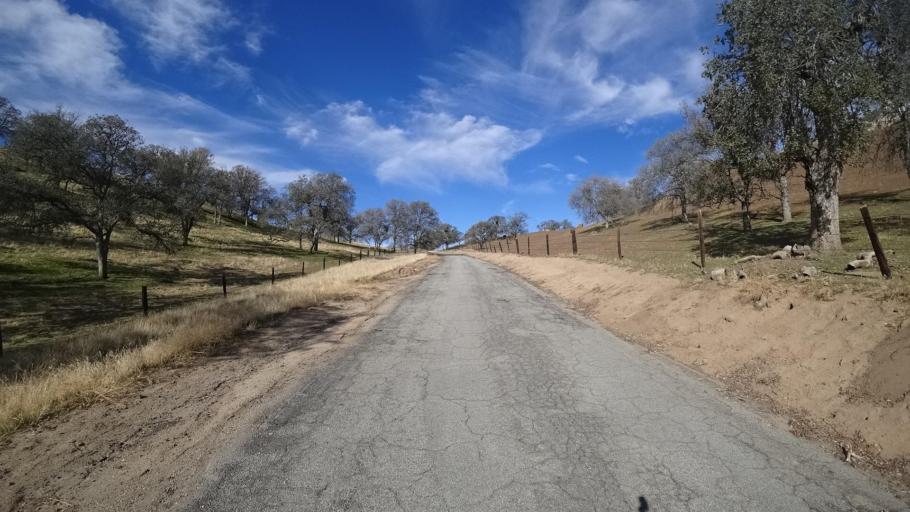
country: US
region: California
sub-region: Kern County
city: Oildale
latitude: 35.5655
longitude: -118.7970
